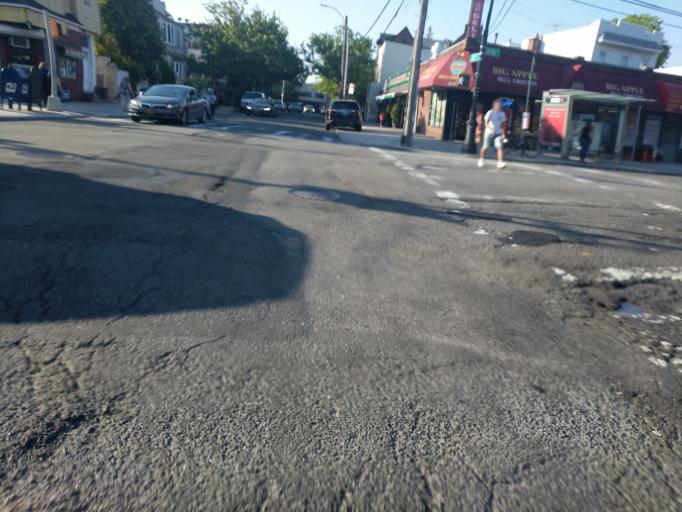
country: US
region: New York
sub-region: Queens County
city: Long Island City
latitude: 40.7218
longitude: -73.9044
